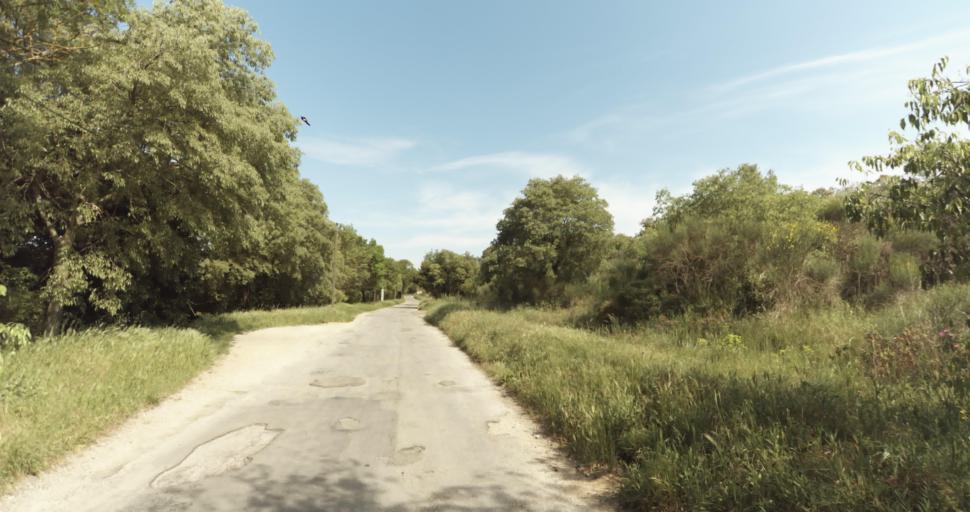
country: FR
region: Languedoc-Roussillon
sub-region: Departement du Gard
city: Rodilhan
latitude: 43.8599
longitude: 4.3947
